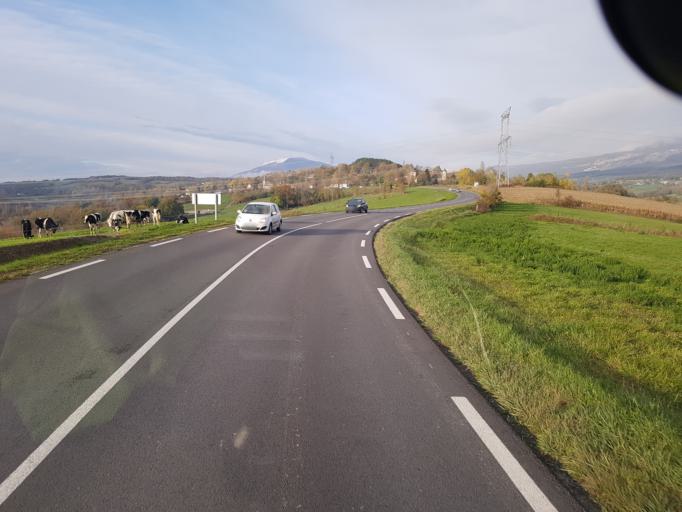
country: FR
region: Rhone-Alpes
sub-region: Departement de la Haute-Savoie
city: Frangy
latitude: 46.0355
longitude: 5.8880
